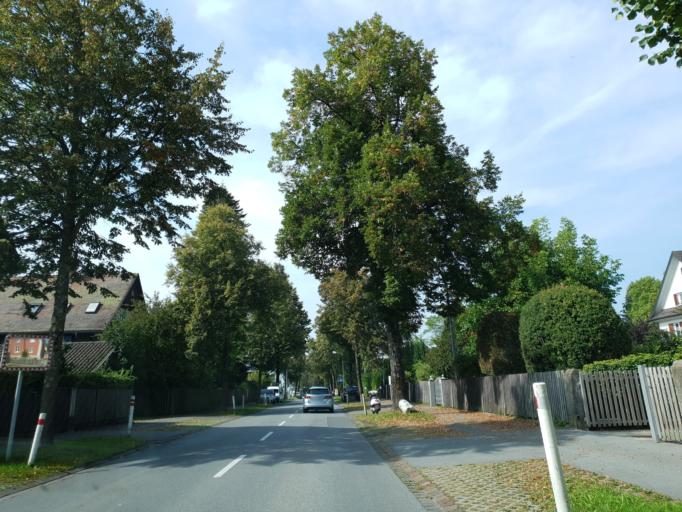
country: AT
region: Vorarlberg
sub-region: Politischer Bezirk Bregenz
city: Bregenz
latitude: 47.4955
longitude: 9.7376
